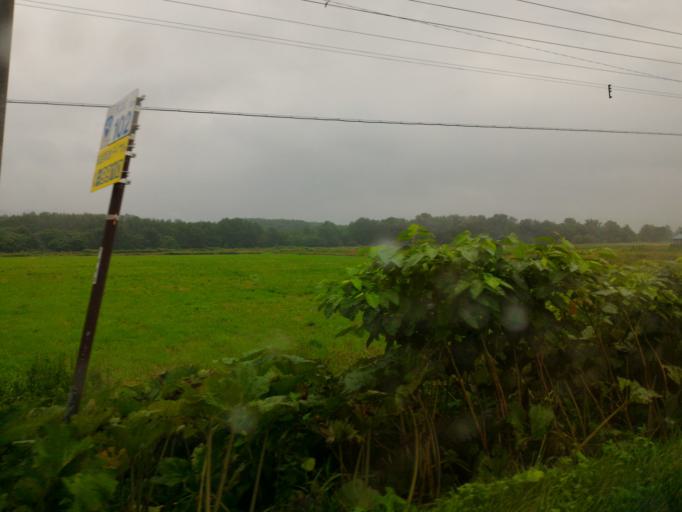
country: JP
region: Hokkaido
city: Nayoro
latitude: 44.5188
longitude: 142.3286
